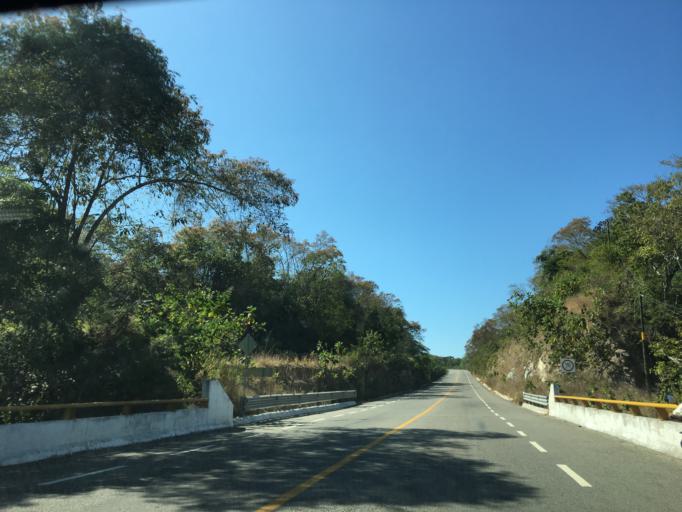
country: MX
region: Oaxaca
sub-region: Santa Maria Huatulco
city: Sector H Tres
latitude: 15.7742
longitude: -96.2350
